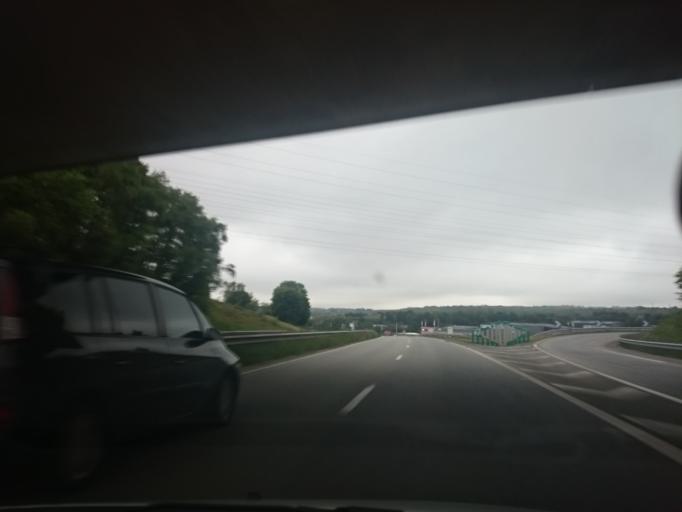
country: FR
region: Brittany
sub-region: Departement du Finistere
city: Ergue-Gaberic
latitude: 48.0000
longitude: -4.0502
